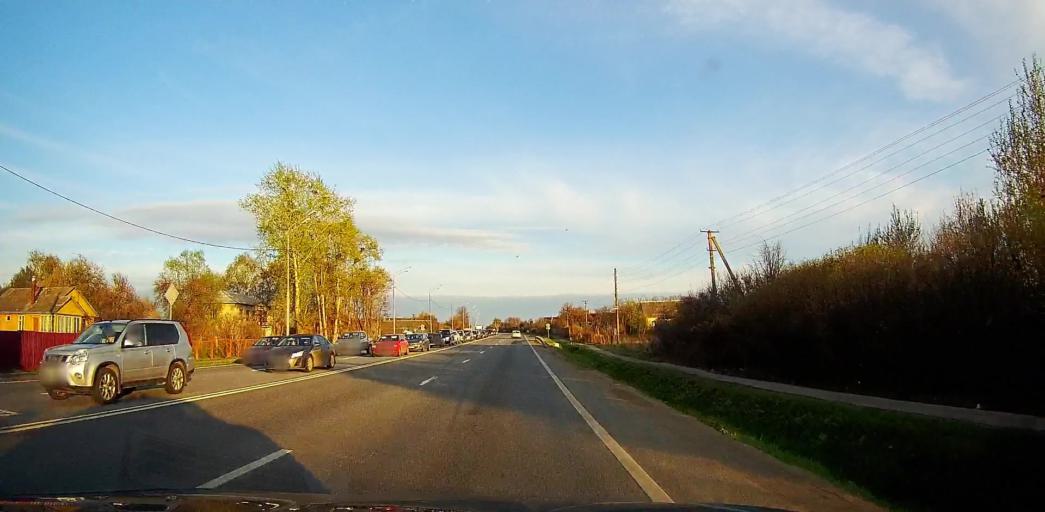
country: RU
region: Moskovskaya
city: Troitskoye
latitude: 55.2471
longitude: 38.5293
